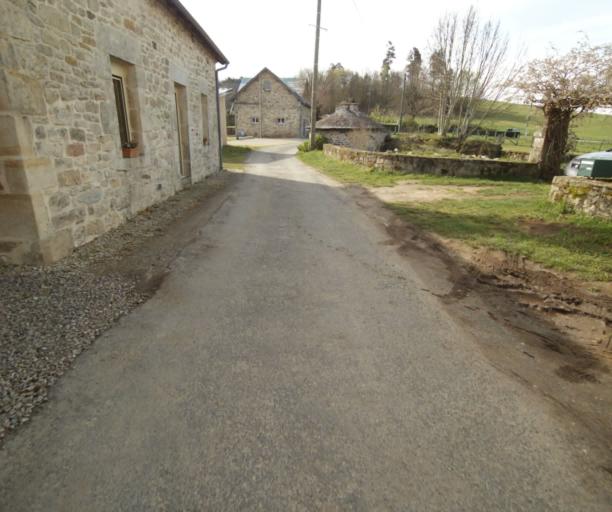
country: FR
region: Limousin
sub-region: Departement de la Correze
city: Correze
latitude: 45.3411
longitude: 1.8319
